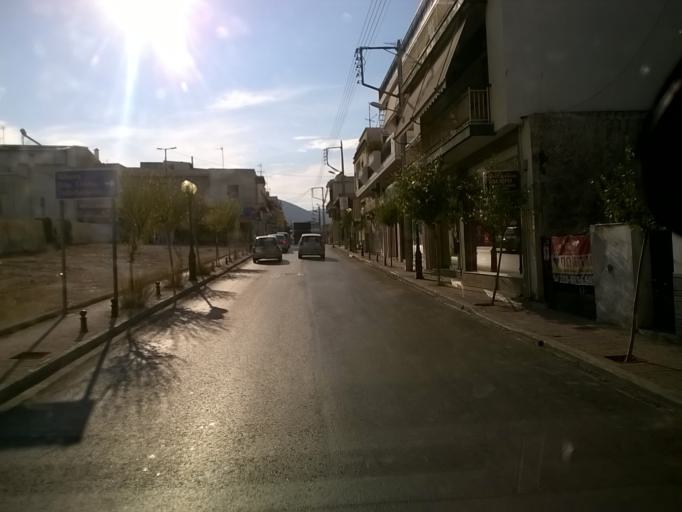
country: GR
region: Attica
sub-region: Nomarchia Athinas
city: Agios Dimitrios
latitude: 37.9386
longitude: 23.7303
